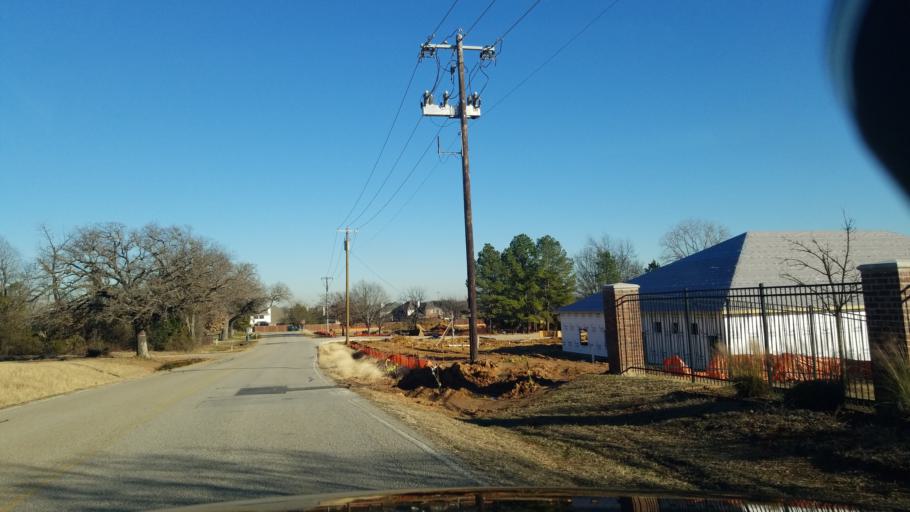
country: US
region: Texas
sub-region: Denton County
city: Corinth
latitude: 33.1545
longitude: -97.0548
